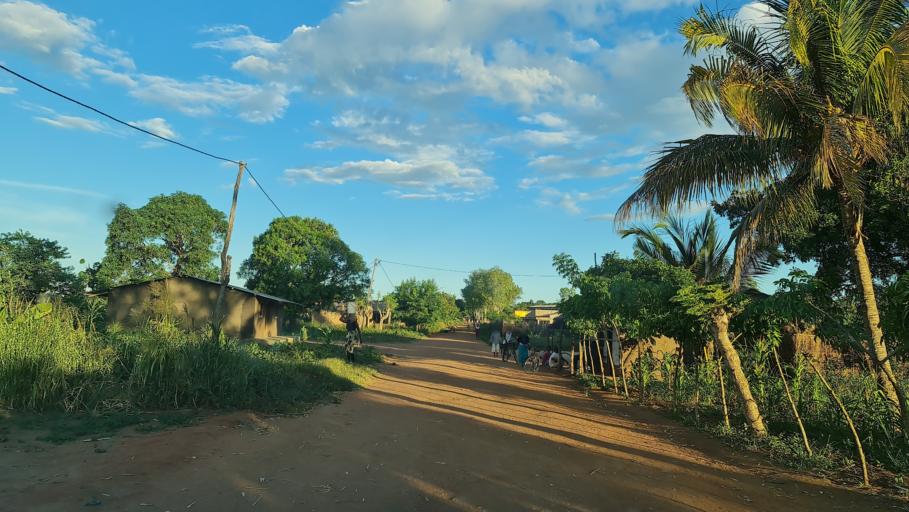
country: MZ
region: Nampula
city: Ilha de Mocambique
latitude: -14.9013
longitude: 40.1365
